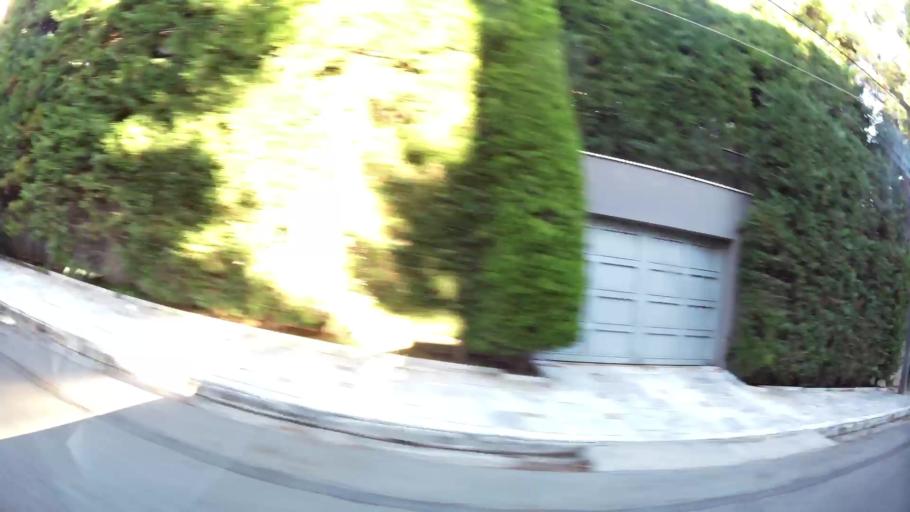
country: GR
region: Attica
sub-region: Nomarchia Athinas
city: Nea Erythraia
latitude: 38.0868
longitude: 23.8289
